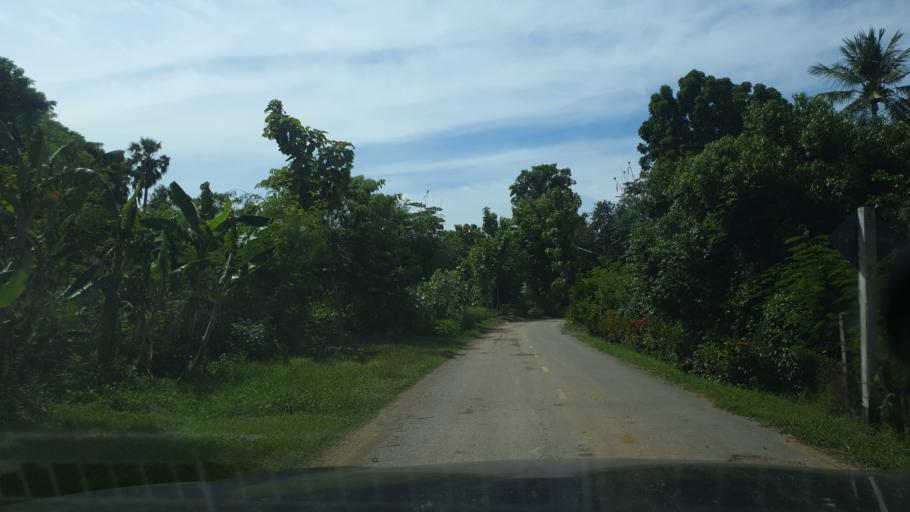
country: TH
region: Sukhothai
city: Sawankhalok
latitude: 17.2171
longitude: 99.7177
